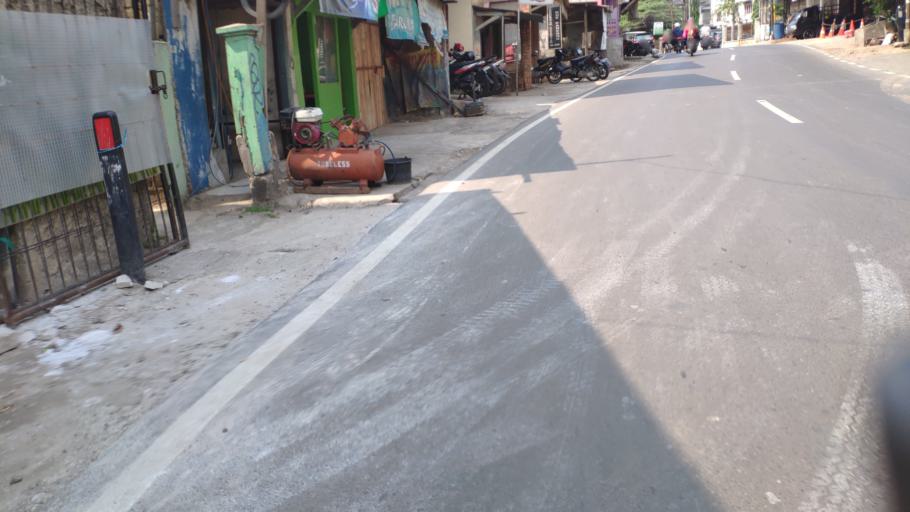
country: ID
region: West Java
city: Pamulang
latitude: -6.3173
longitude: 106.8117
